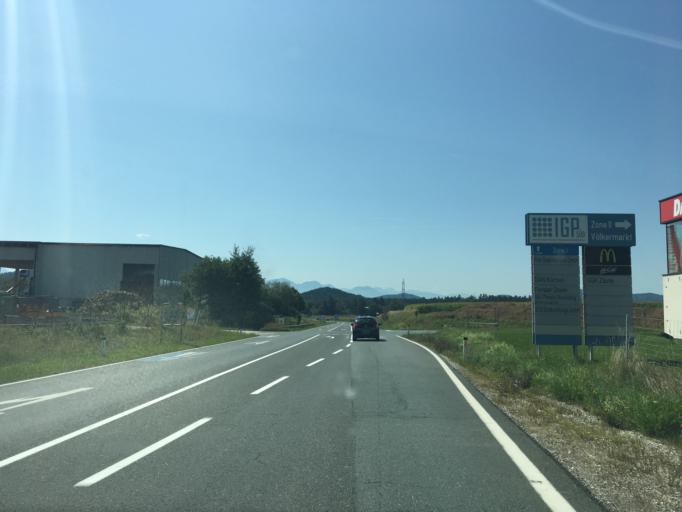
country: AT
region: Carinthia
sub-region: Politischer Bezirk Volkermarkt
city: Voelkermarkt
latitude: 46.6818
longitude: 14.6785
